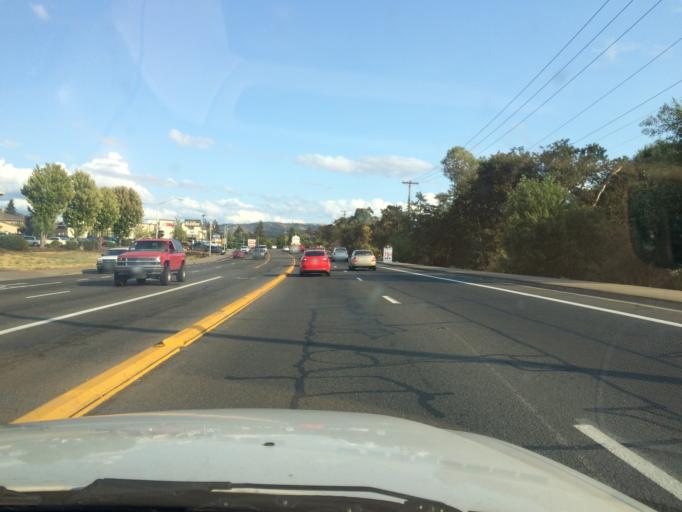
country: US
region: Oregon
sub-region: Douglas County
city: Roseburg
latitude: 43.2317
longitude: -123.3731
